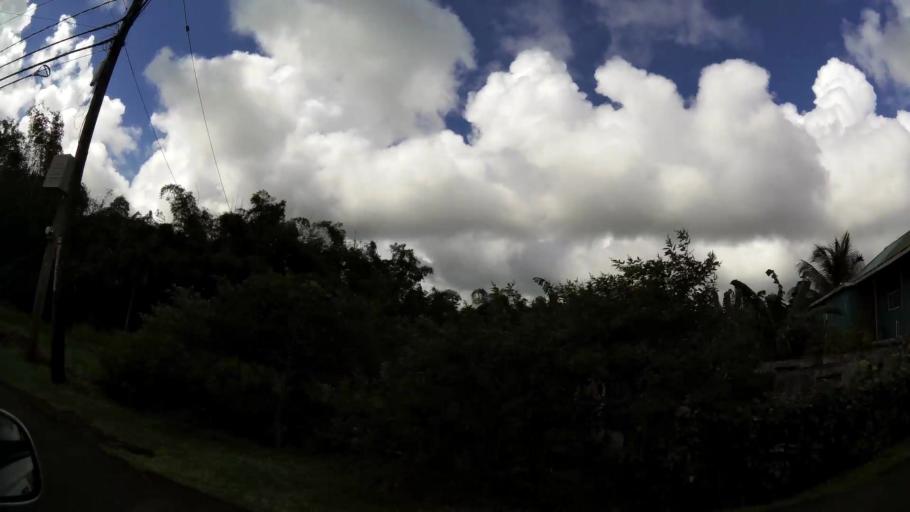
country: GD
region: Saint Andrew
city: Grenville
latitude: 12.1212
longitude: -61.6677
